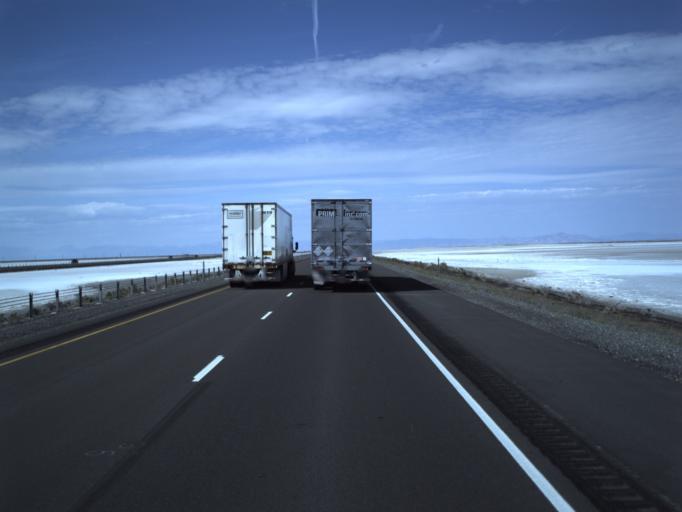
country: US
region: Utah
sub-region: Tooele County
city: Wendover
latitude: 40.7297
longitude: -113.4113
